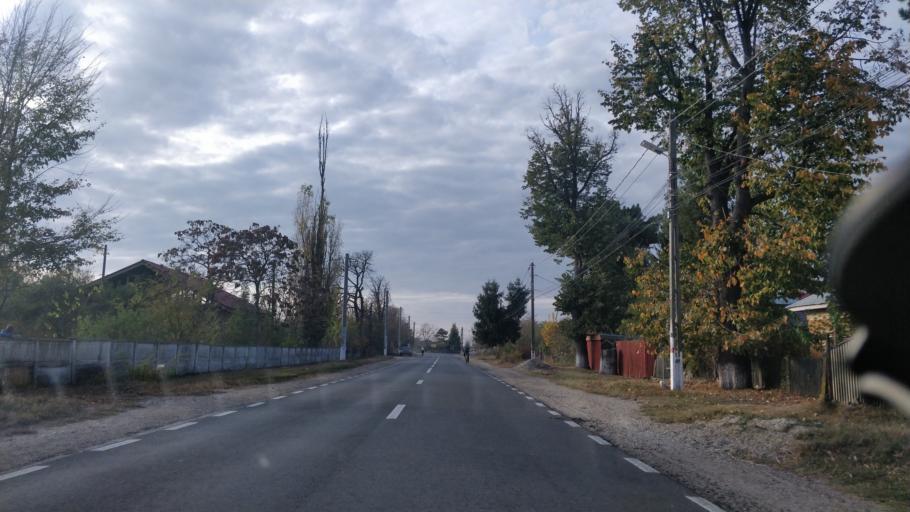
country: RO
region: Giurgiu
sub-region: Comuna Clejani
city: Clejani
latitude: 44.3426
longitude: 25.6736
